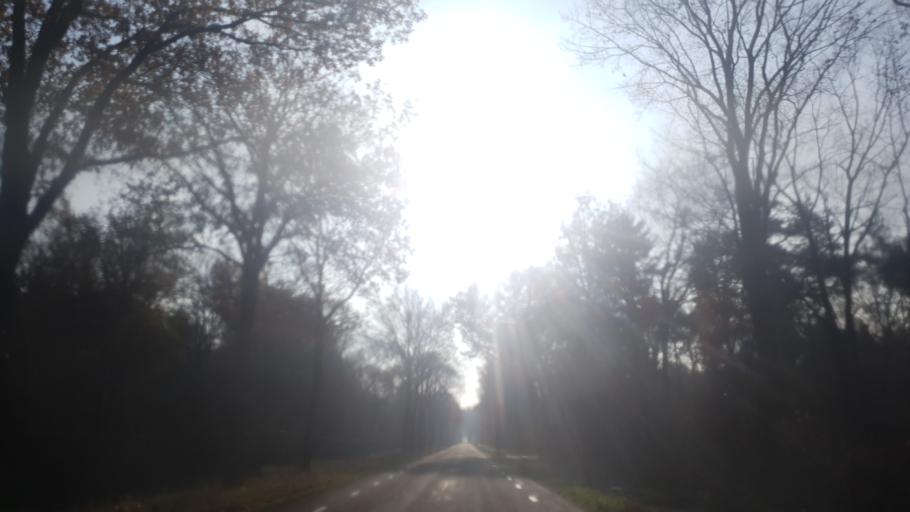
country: NL
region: North Brabant
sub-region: Gemeente Landerd
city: Reek
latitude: 51.7302
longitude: 5.6821
